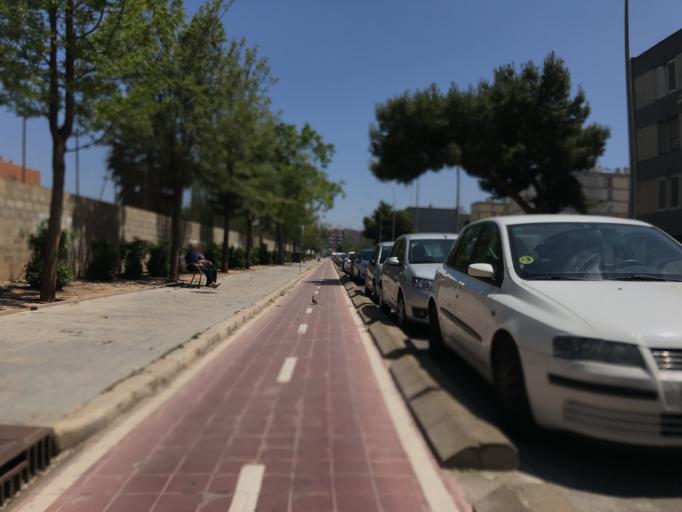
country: ES
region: Valencia
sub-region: Provincia de Valencia
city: Mislata
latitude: 39.4661
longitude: -0.4000
